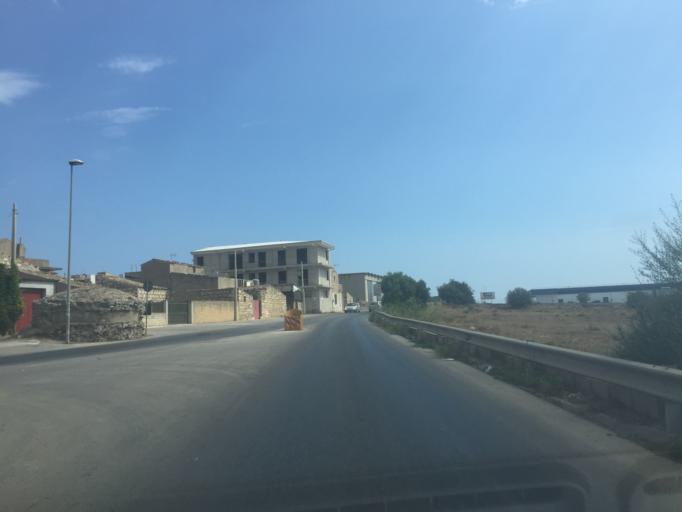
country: IT
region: Sicily
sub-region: Ragusa
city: Santa Croce Camerina
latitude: 36.8284
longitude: 14.5192
